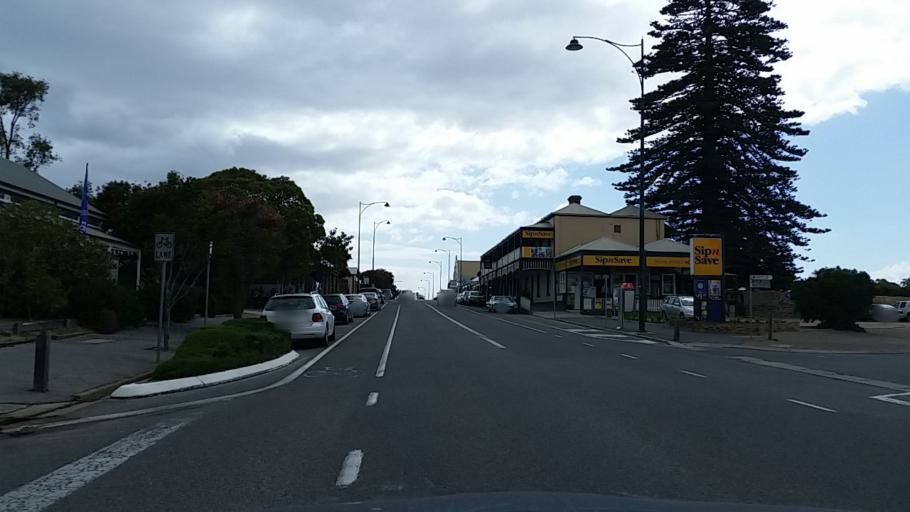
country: AU
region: South Australia
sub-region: Alexandrina
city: Port Elliot
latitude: -35.5301
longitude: 138.6822
